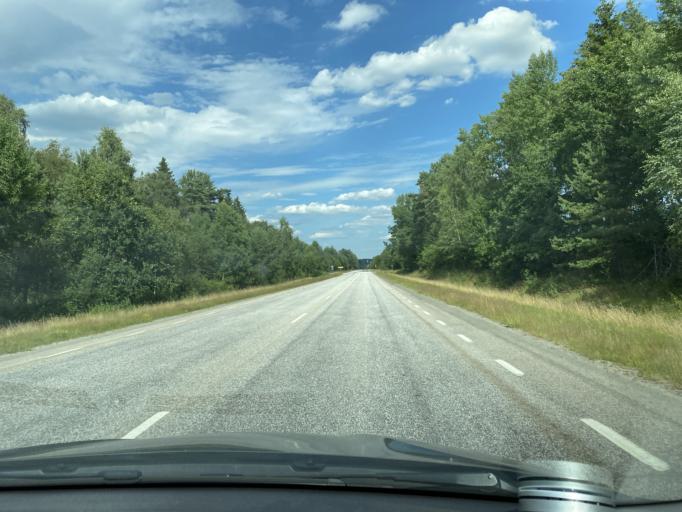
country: SE
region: Kronoberg
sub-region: Markaryds Kommun
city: Markaryd
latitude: 56.4341
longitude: 13.5725
